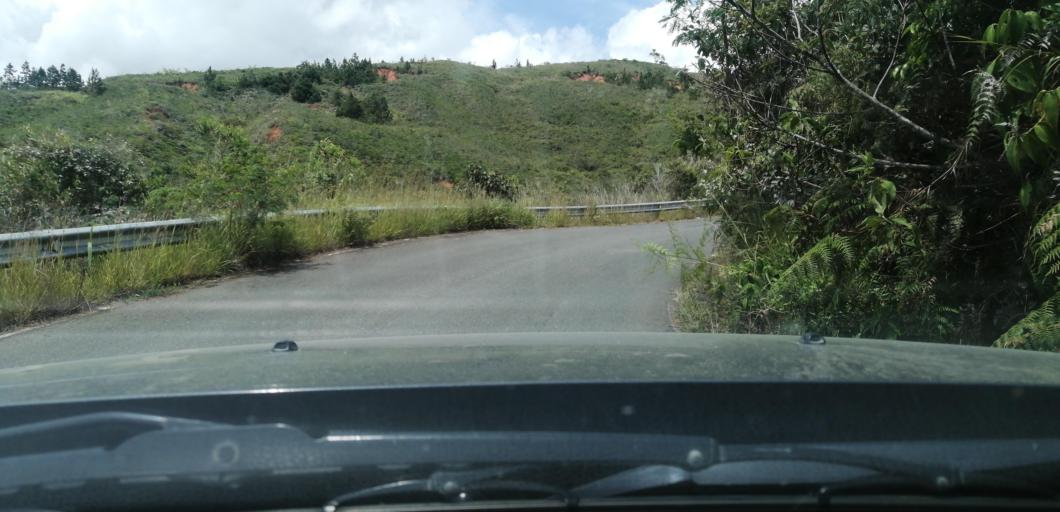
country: CO
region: Valle del Cauca
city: Dagua
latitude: 3.7127
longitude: -76.5848
